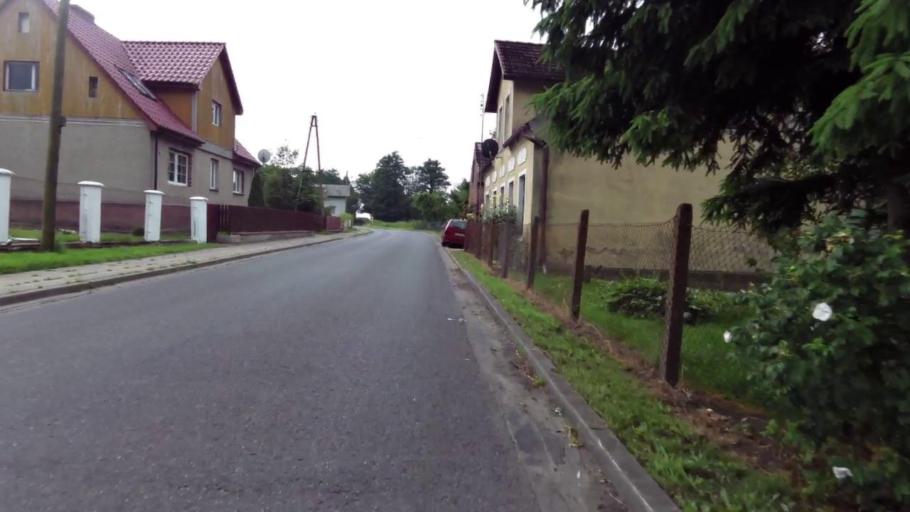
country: PL
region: West Pomeranian Voivodeship
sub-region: Powiat kamienski
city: Wolin
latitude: 53.8376
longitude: 14.6255
